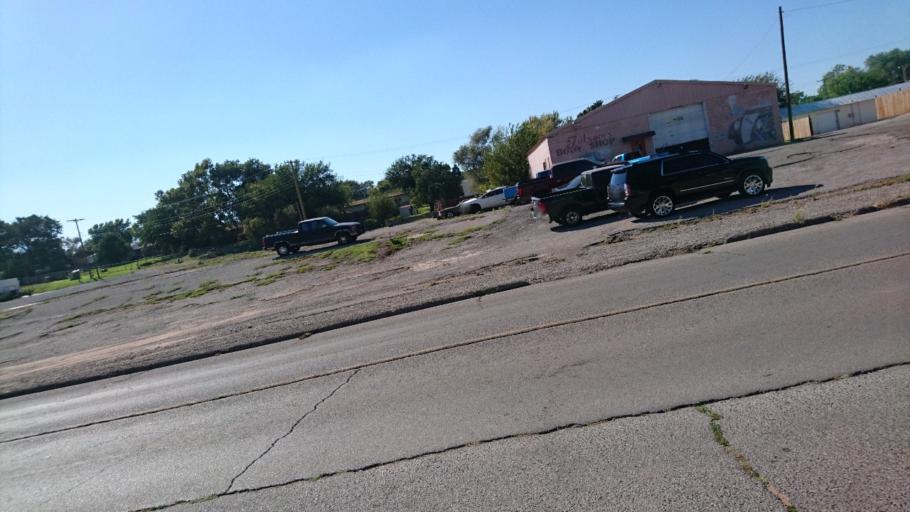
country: US
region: Oklahoma
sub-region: Custer County
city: Clinton
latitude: 35.5042
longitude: -98.9720
